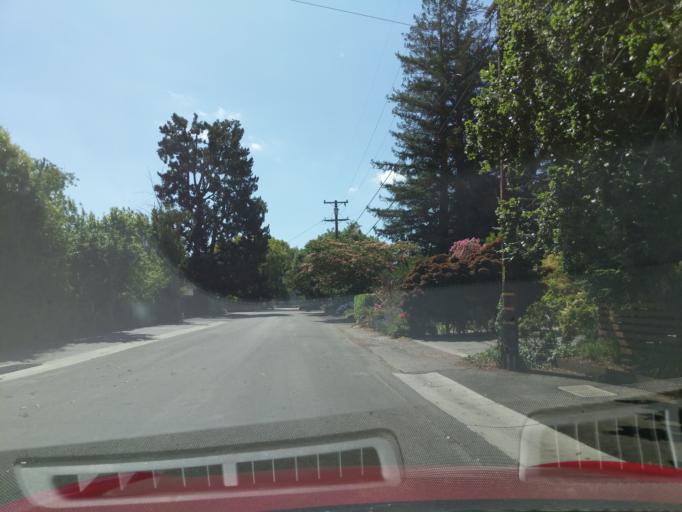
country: US
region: California
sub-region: San Mateo County
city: West Menlo Park
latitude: 37.4361
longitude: -122.1932
